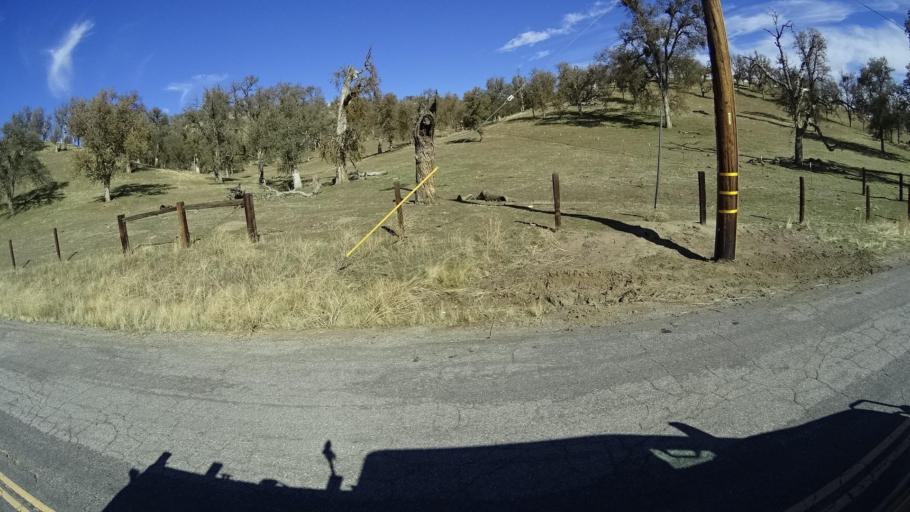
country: US
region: California
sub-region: Kern County
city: Alta Sierra
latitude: 35.6309
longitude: -118.7724
